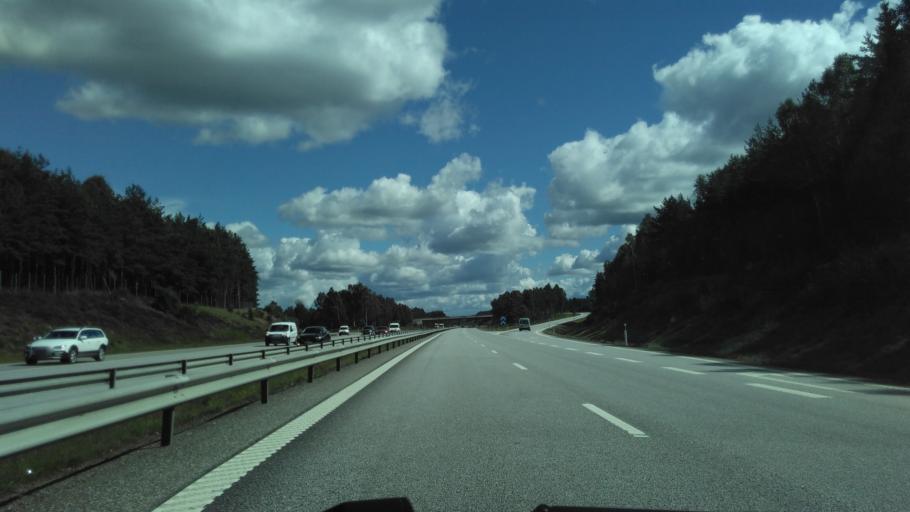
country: SE
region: Vaestra Goetaland
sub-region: Harryda Kommun
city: Hindas
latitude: 57.6761
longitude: 12.3453
